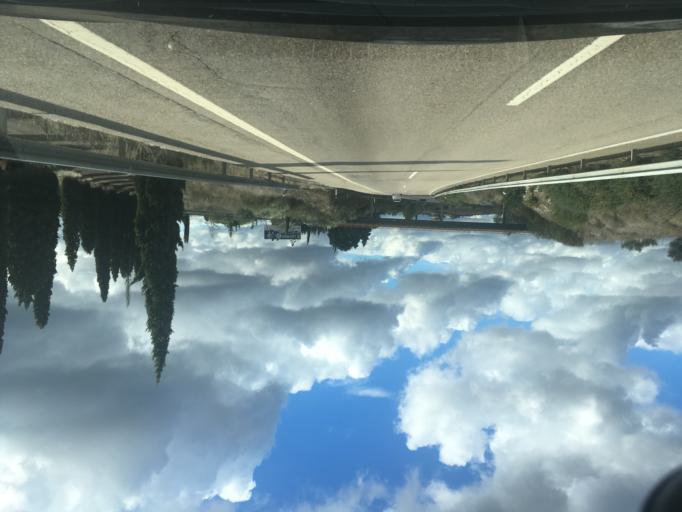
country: PT
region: Santarem
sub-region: Torres Novas
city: Torres Novas
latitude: 39.4717
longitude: -8.5937
